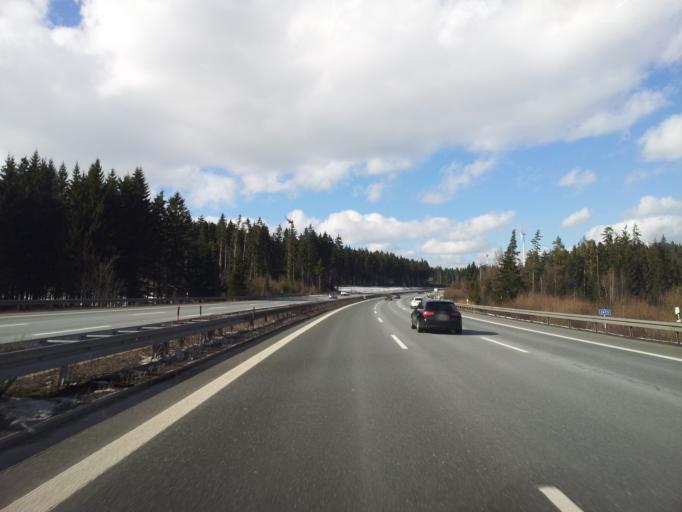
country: DE
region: Bavaria
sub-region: Upper Franconia
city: Munchberg
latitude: 50.2301
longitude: 11.7780
